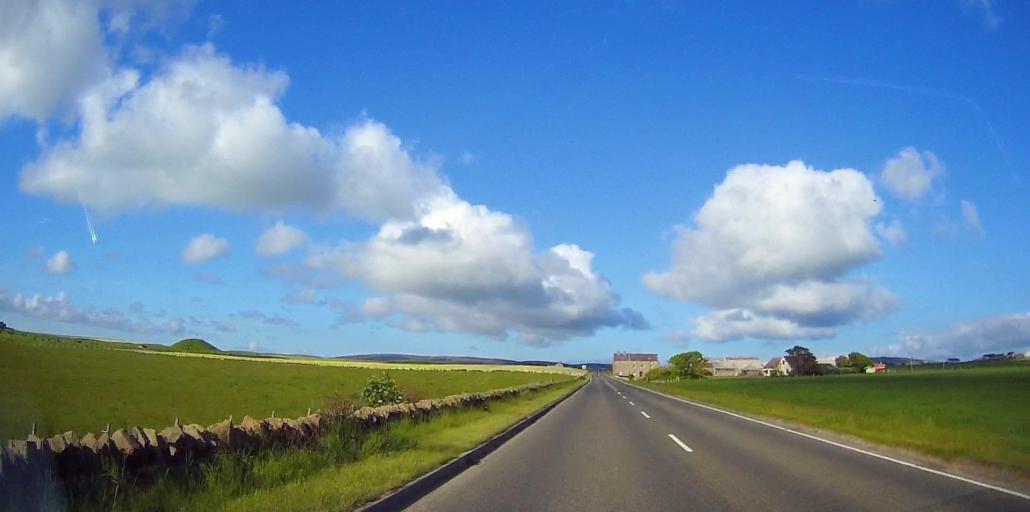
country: GB
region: Scotland
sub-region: Orkney Islands
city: Stromness
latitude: 58.9931
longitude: -3.1909
